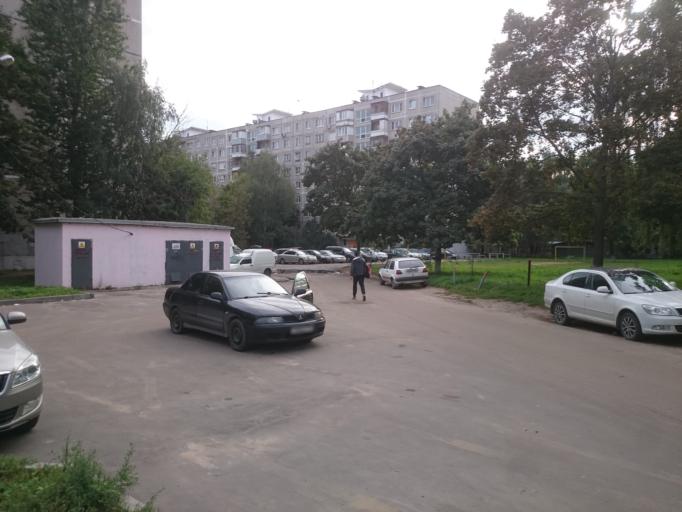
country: RU
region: Moskovskaya
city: Balashikha
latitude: 55.7970
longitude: 37.9790
